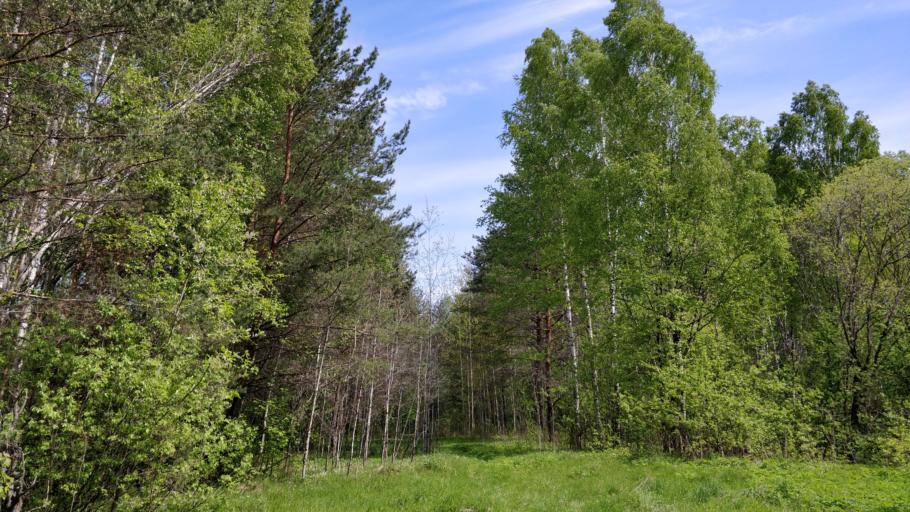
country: RU
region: Perm
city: Kondratovo
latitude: 57.9870
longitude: 56.1382
